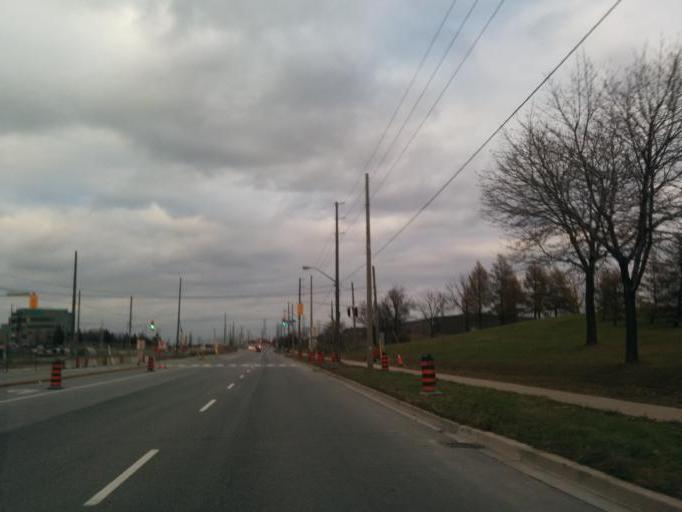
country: CA
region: Ontario
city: Etobicoke
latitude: 43.6591
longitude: -79.5946
